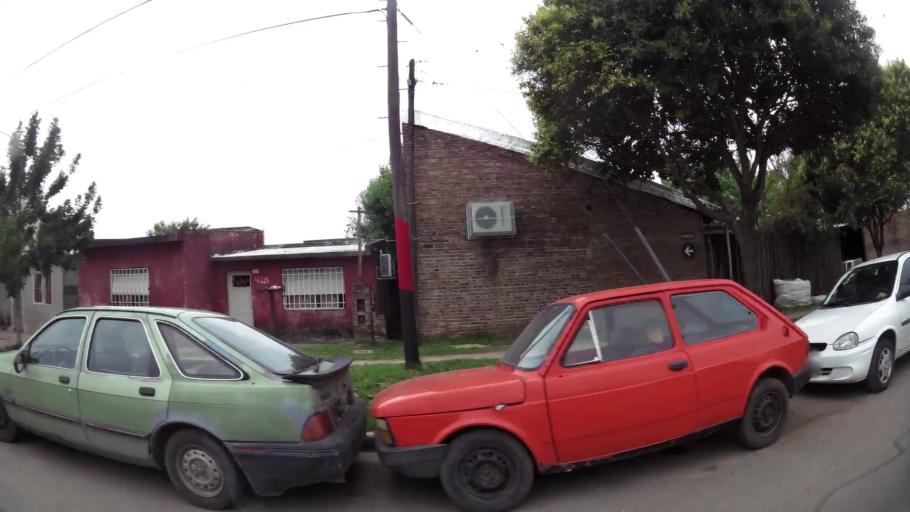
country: AR
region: Santa Fe
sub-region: Departamento de Rosario
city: Rosario
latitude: -32.9854
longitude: -60.6596
